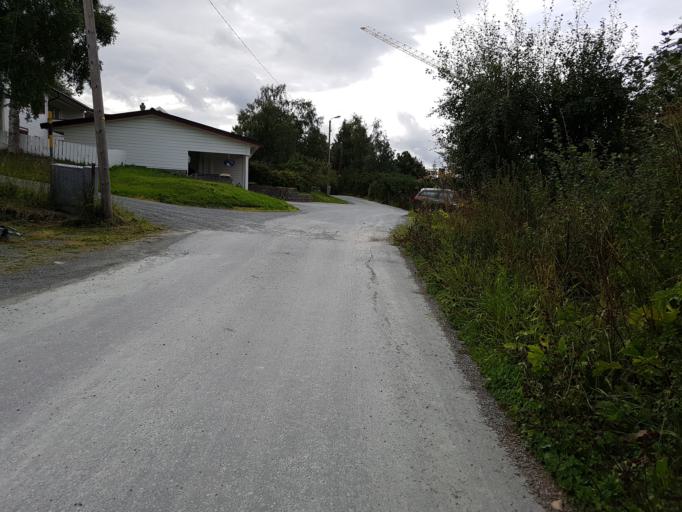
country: NO
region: Sor-Trondelag
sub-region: Trondheim
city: Trondheim
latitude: 63.4175
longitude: 10.4691
